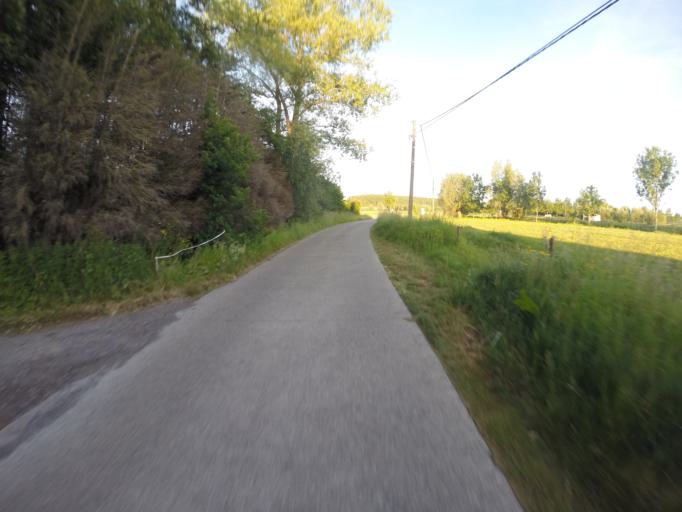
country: BE
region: Flanders
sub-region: Provincie Oost-Vlaanderen
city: Aalter
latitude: 51.1215
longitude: 3.4811
